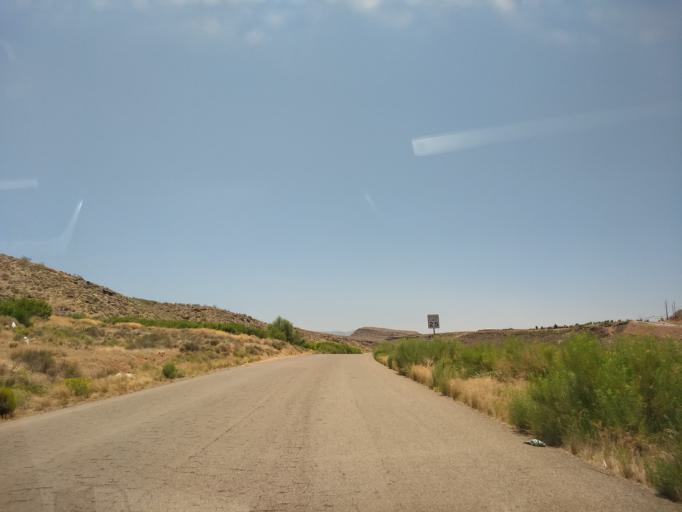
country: US
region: Utah
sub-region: Washington County
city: Washington
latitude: 37.1412
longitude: -113.4584
